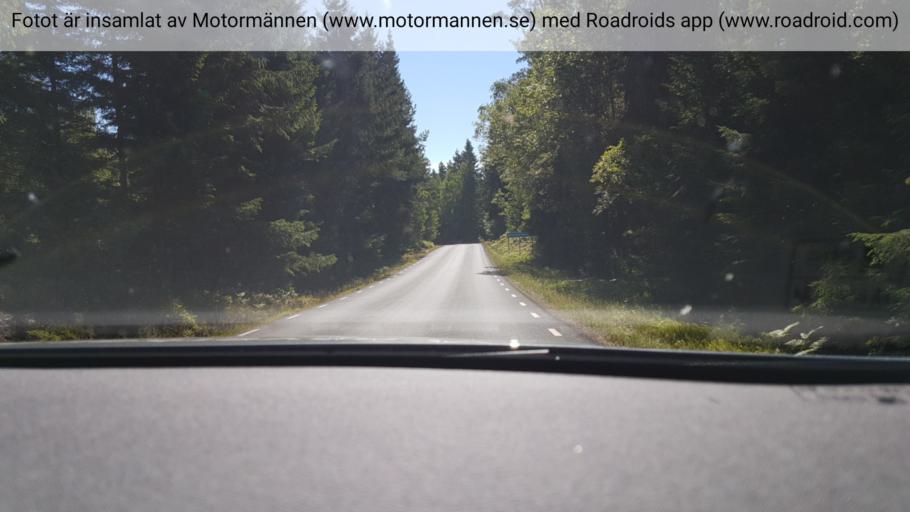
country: SE
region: Vaestra Goetaland
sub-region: Tidaholms Kommun
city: Tidaholm
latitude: 58.1027
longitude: 14.0802
